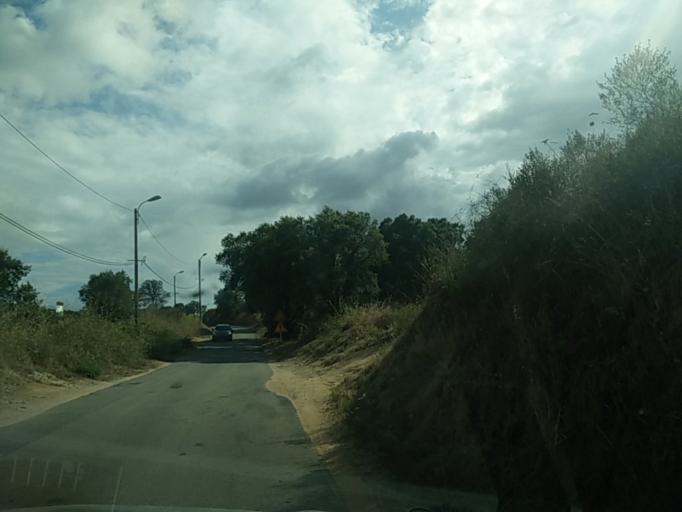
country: FR
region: Corsica
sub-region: Departement de la Corse-du-Sud
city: Alata
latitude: 41.9476
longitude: 8.7722
